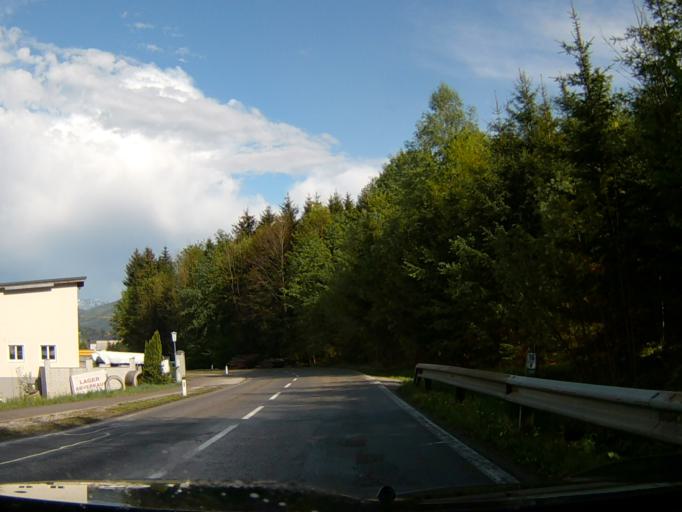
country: AT
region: Upper Austria
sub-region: Politischer Bezirk Vocklabruck
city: Mondsee
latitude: 47.8466
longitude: 13.3312
